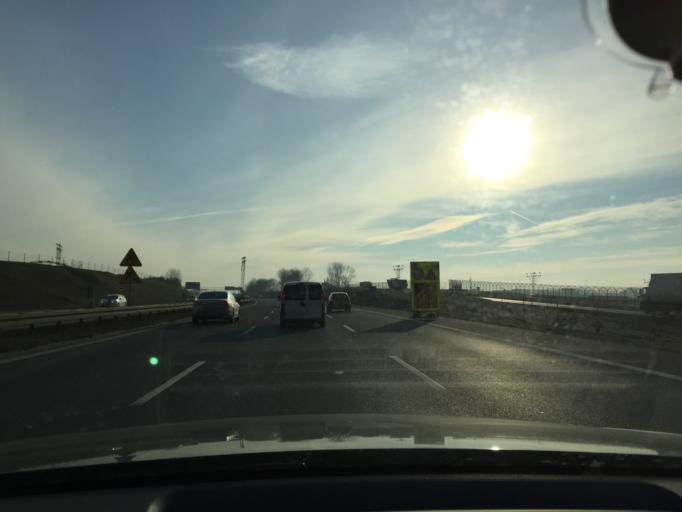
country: PL
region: Lesser Poland Voivodeship
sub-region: Powiat krakowski
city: Balice
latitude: 50.0819
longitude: 19.8081
